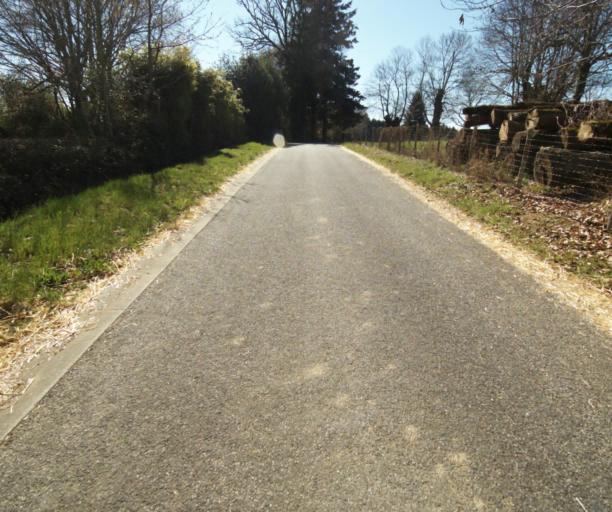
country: FR
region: Limousin
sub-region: Departement de la Correze
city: Chamboulive
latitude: 45.4266
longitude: 1.7088
